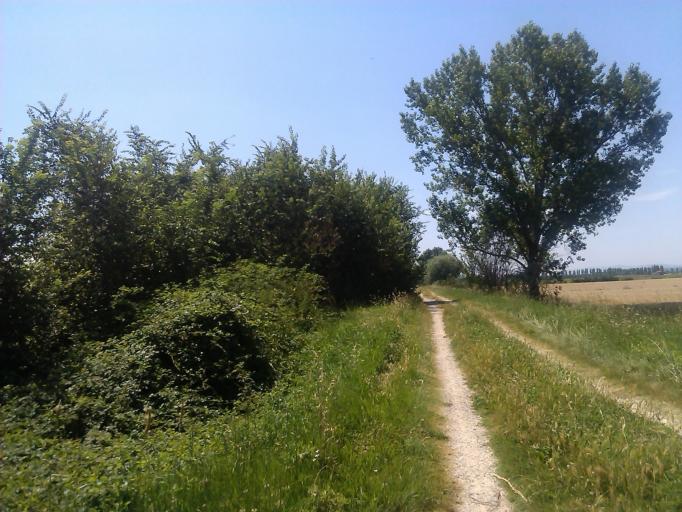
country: IT
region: Tuscany
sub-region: Province of Arezzo
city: Cesa
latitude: 43.3404
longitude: 11.8278
